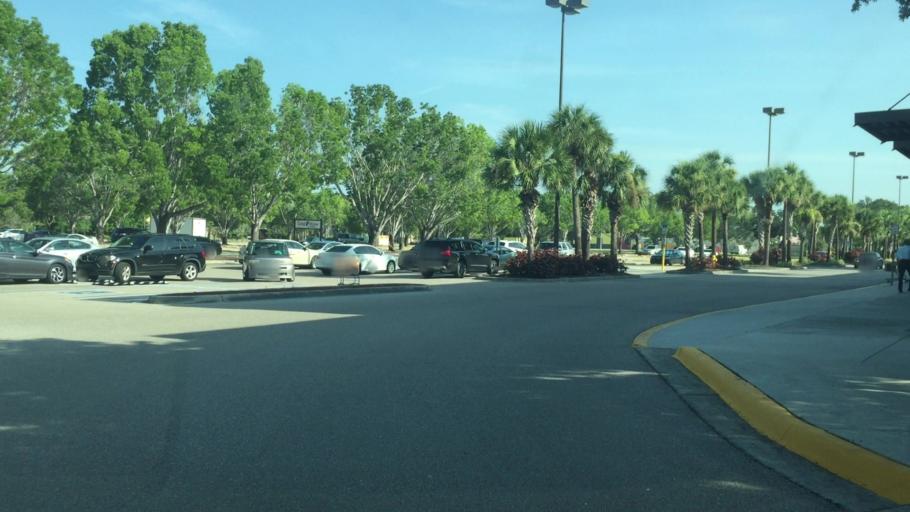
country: US
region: Florida
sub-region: Lee County
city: Villas
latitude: 26.5437
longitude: -81.8689
